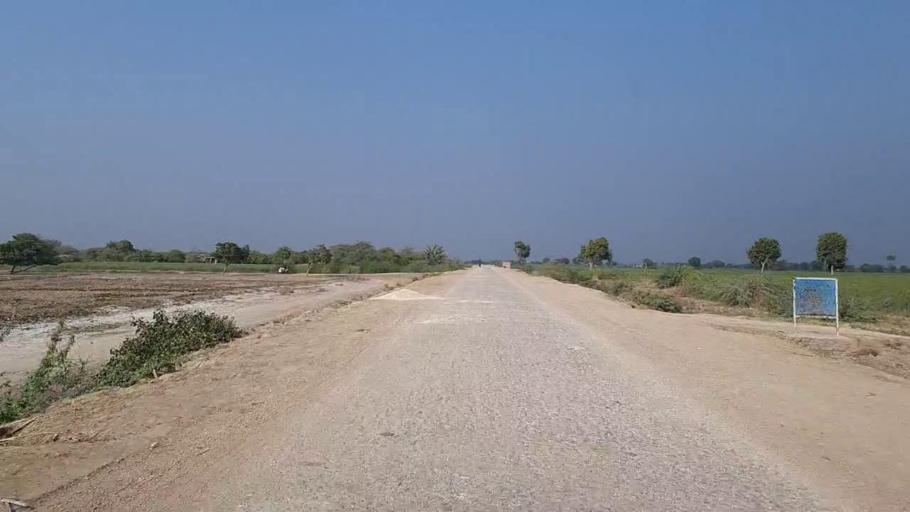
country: PK
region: Sindh
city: Mirwah Gorchani
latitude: 25.4032
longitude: 69.1400
